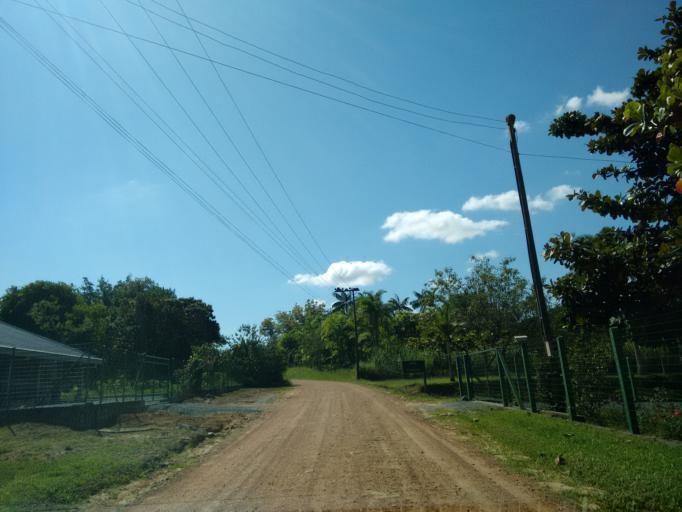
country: BR
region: Santa Catarina
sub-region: Indaial
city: Indaial
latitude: -26.9157
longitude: -49.1908
